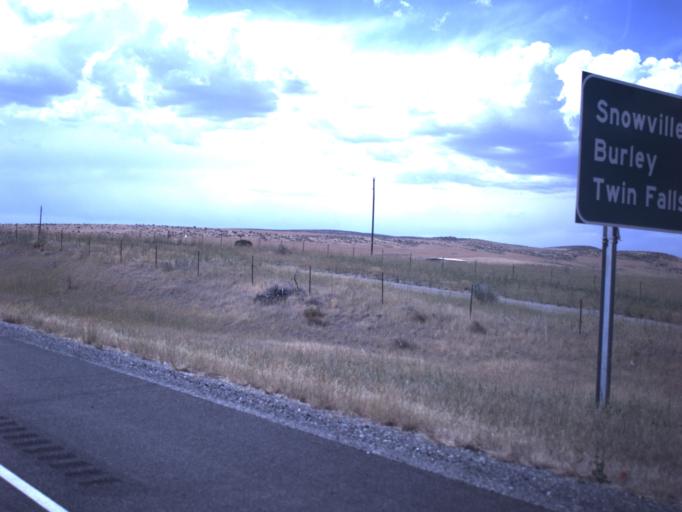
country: US
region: Idaho
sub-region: Oneida County
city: Malad City
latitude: 41.9068
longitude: -112.5874
